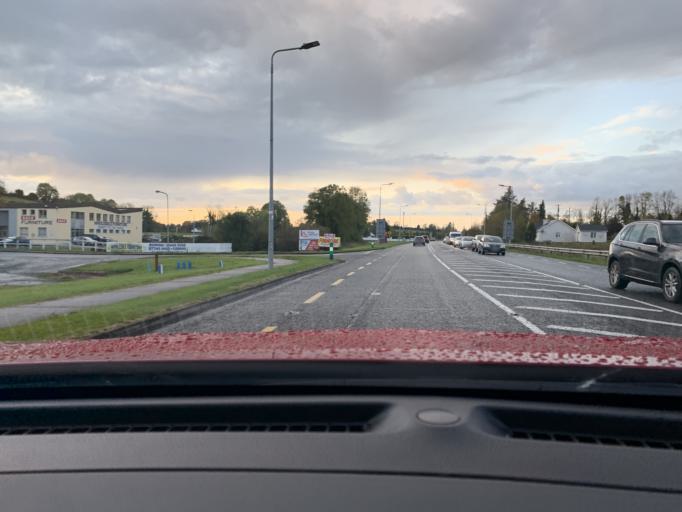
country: IE
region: Connaught
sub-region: County Leitrim
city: Carrick-on-Shannon
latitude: 53.9435
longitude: -8.1123
